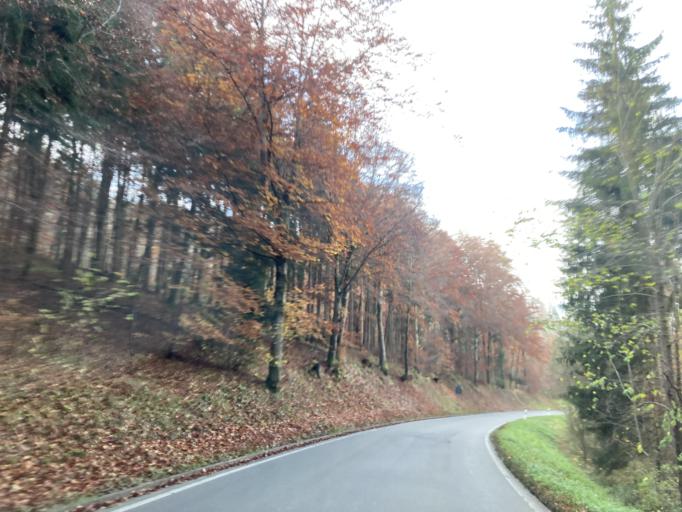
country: DE
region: Baden-Wuerttemberg
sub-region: Tuebingen Region
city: Haigerloch
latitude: 48.4416
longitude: 8.7928
